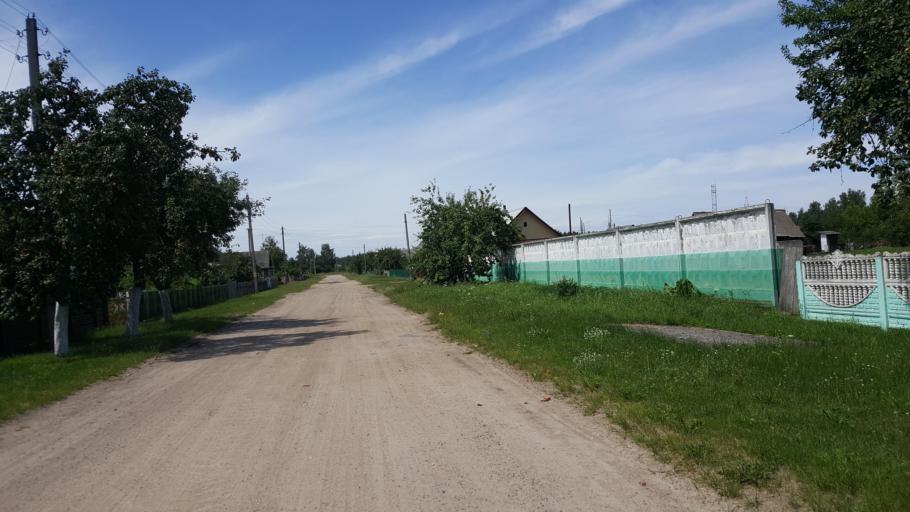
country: BY
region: Brest
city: Pruzhany
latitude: 52.5654
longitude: 24.2112
